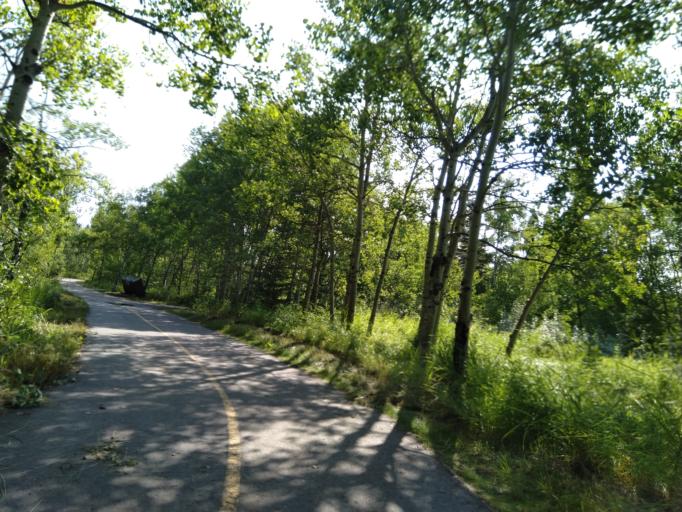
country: CA
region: Alberta
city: Calgary
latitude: 51.0962
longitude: -114.2440
